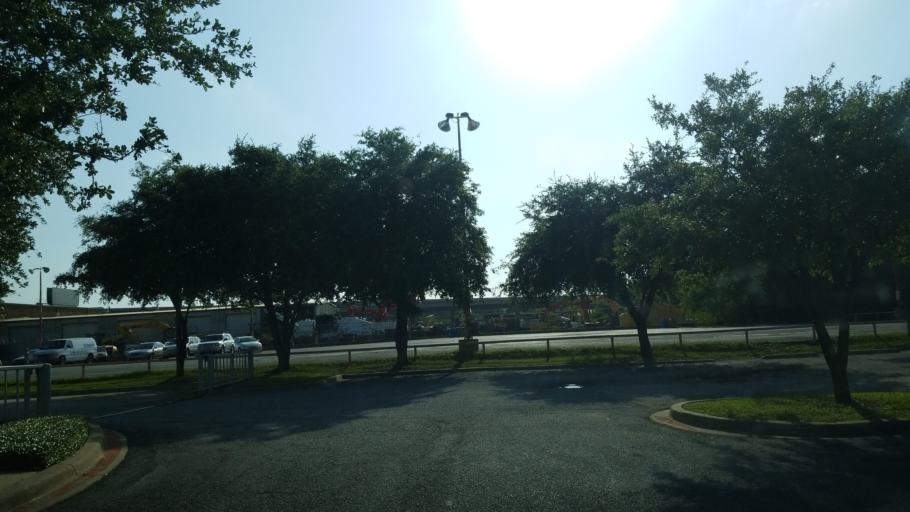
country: US
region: Texas
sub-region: Dallas County
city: Farmers Branch
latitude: 32.8750
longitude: -96.8951
